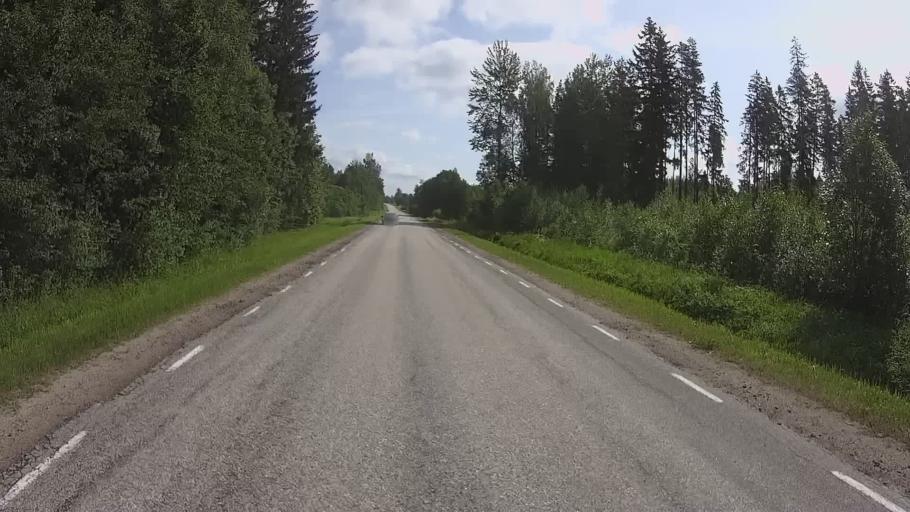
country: EE
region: Vorumaa
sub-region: Antsla vald
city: Vana-Antsla
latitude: 57.8484
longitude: 26.5740
